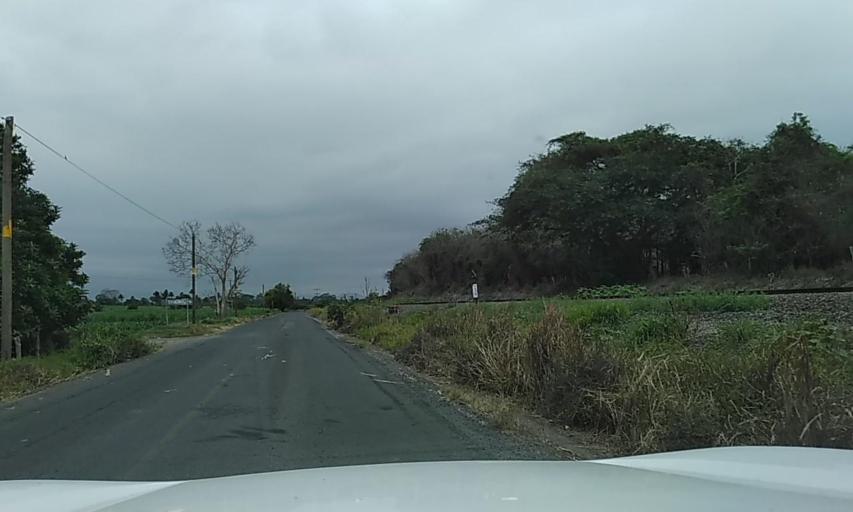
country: MX
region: Veracruz
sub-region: La Antigua
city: Nicolas Blanco (San Pancho)
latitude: 19.3031
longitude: -96.3154
